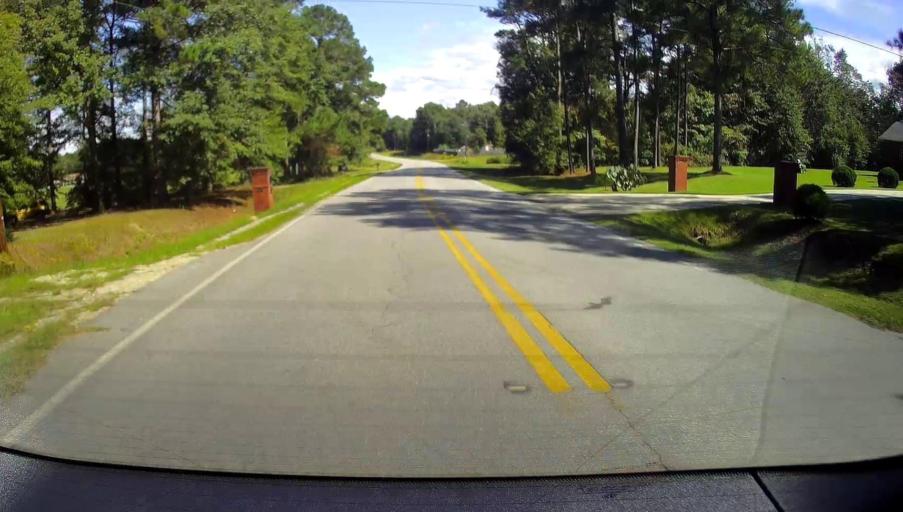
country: US
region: Georgia
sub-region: Houston County
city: Warner Robins
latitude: 32.7142
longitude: -83.5383
